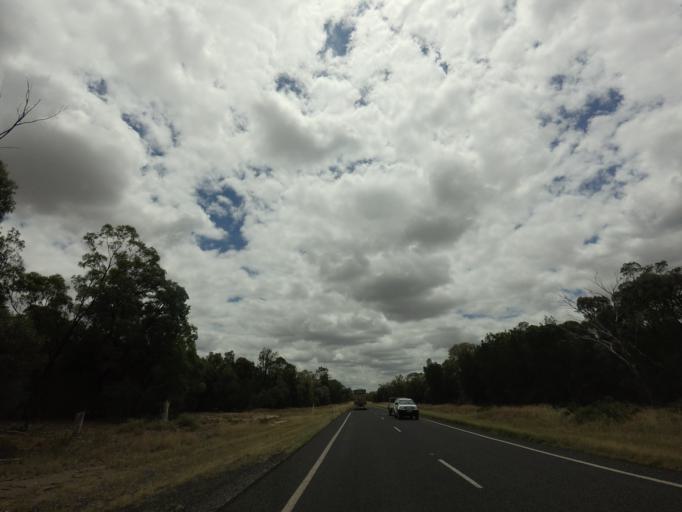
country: AU
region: Queensland
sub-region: Goondiwindi
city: Goondiwindi
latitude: -28.4424
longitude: 150.3002
